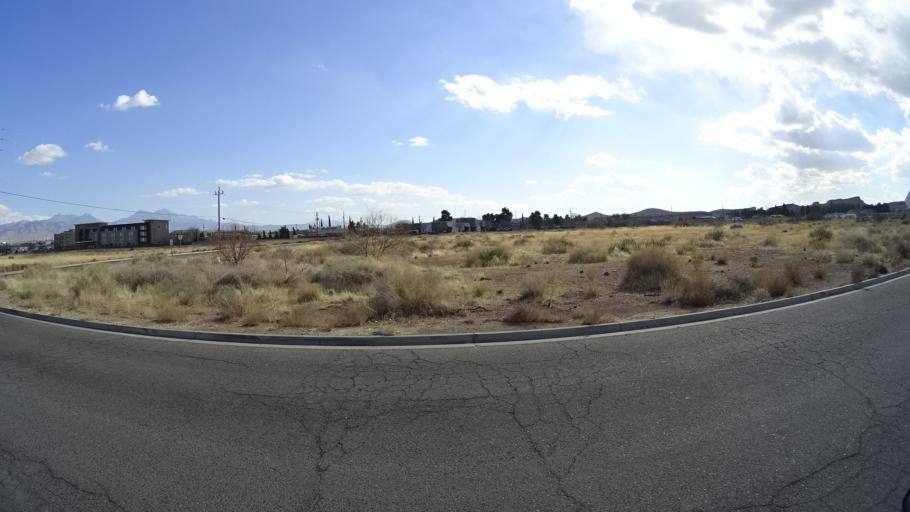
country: US
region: Arizona
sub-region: Mohave County
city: Kingman
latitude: 35.2251
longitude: -114.0407
